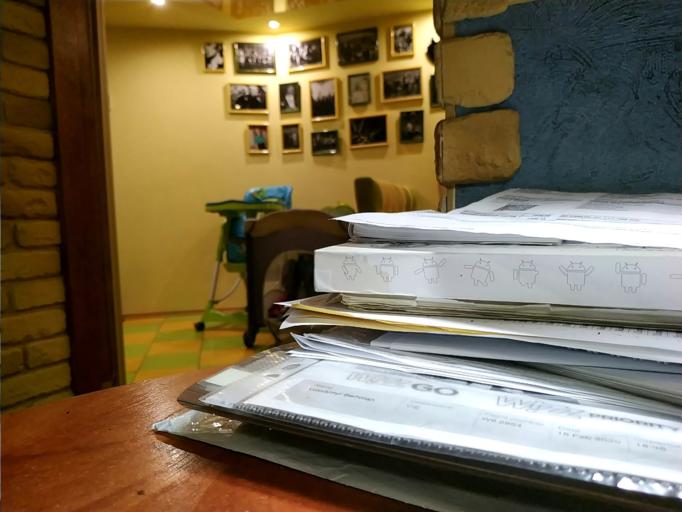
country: RU
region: Arkhangelskaya
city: Kargopol'
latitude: 61.5241
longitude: 39.3091
